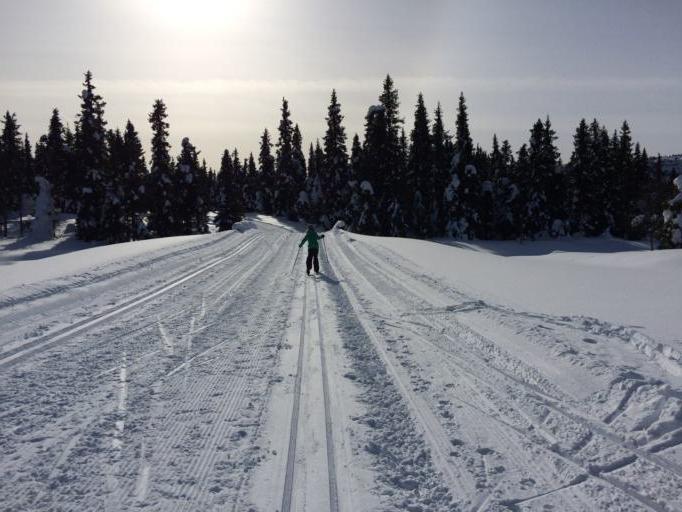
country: NO
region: Oppland
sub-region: Gausdal
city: Segalstad bru
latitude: 61.3280
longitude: 10.0799
